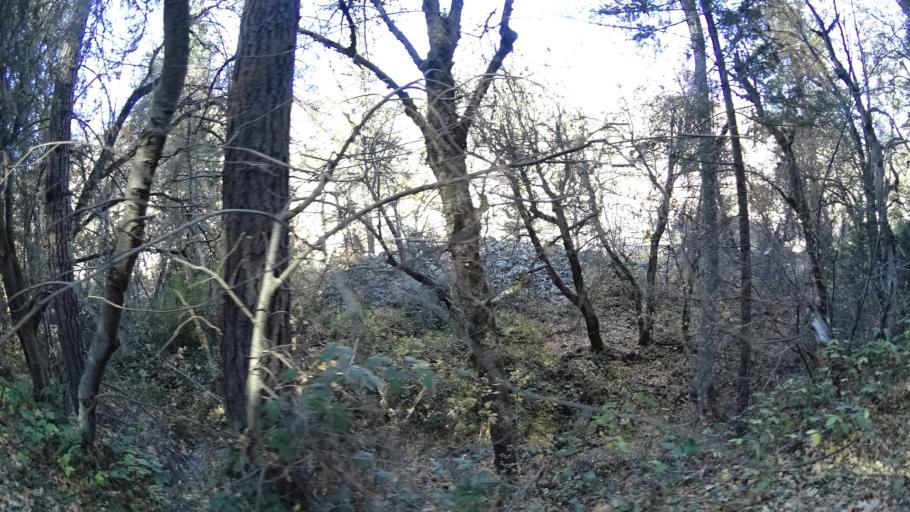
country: US
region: California
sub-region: Siskiyou County
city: Yreka
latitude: 41.8570
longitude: -122.7529
